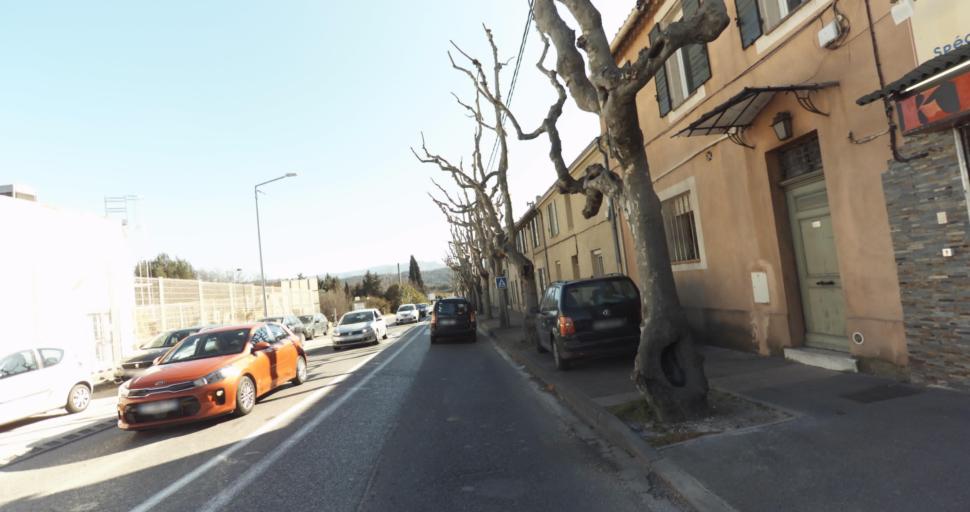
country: FR
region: Provence-Alpes-Cote d'Azur
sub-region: Departement des Bouches-du-Rhone
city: La Bouilladisse
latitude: 43.3892
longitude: 5.5983
